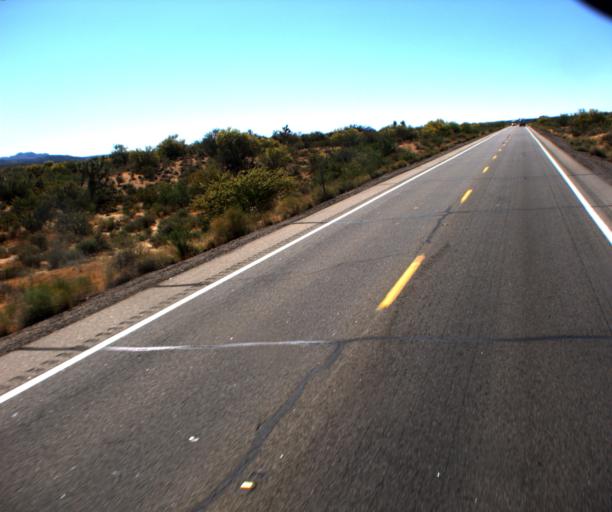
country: US
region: Arizona
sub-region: Yavapai County
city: Bagdad
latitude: 34.3263
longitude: -113.1395
